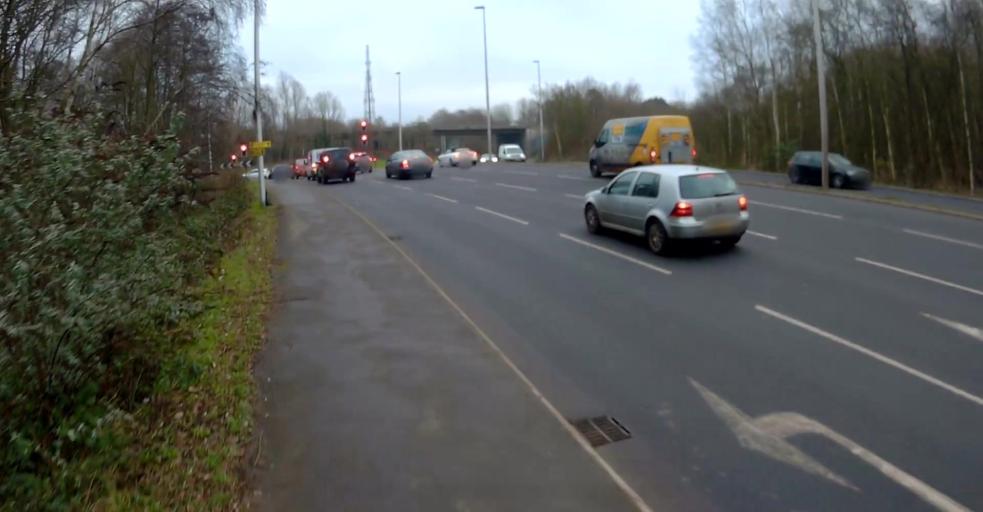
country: GB
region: England
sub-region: Bracknell Forest
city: Binfield
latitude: 51.4124
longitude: -0.8009
